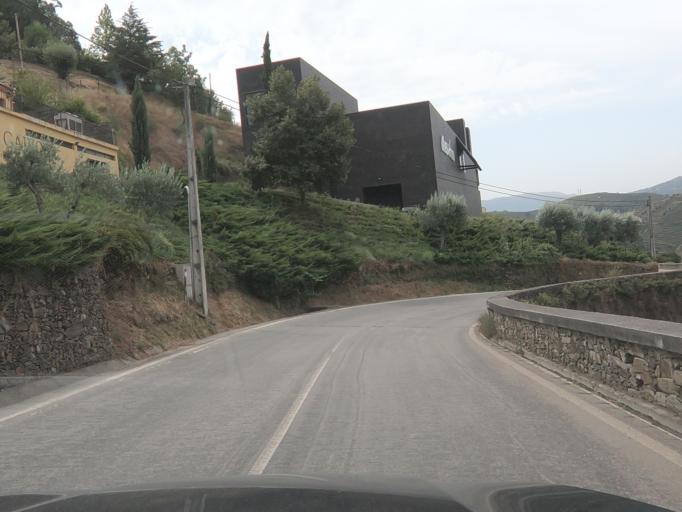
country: PT
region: Vila Real
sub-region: Santa Marta de Penaguiao
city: Santa Marta de Penaguiao
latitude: 41.2328
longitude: -7.7638
